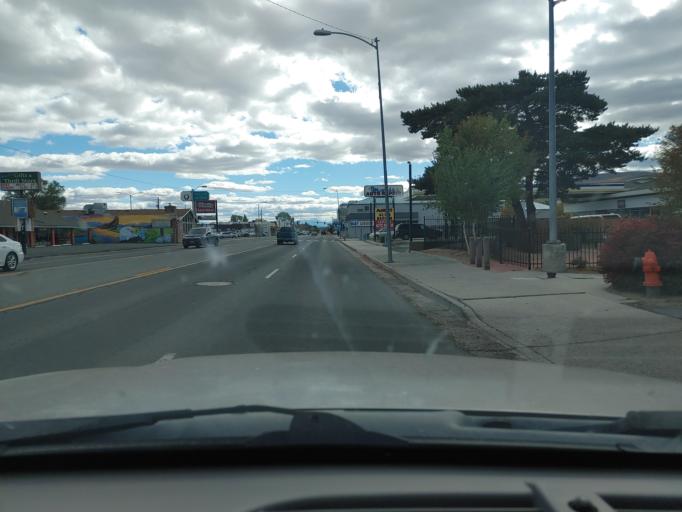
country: US
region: Nevada
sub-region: Carson City
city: Carson City
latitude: 39.1763
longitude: -119.7670
